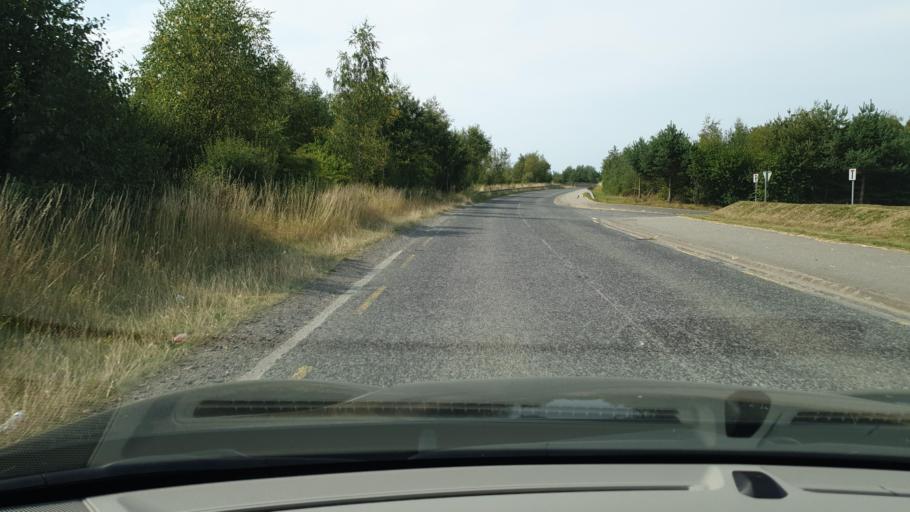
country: IE
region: Leinster
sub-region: An Mhi
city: Dunshaughlin
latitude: 53.5712
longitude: -6.5702
